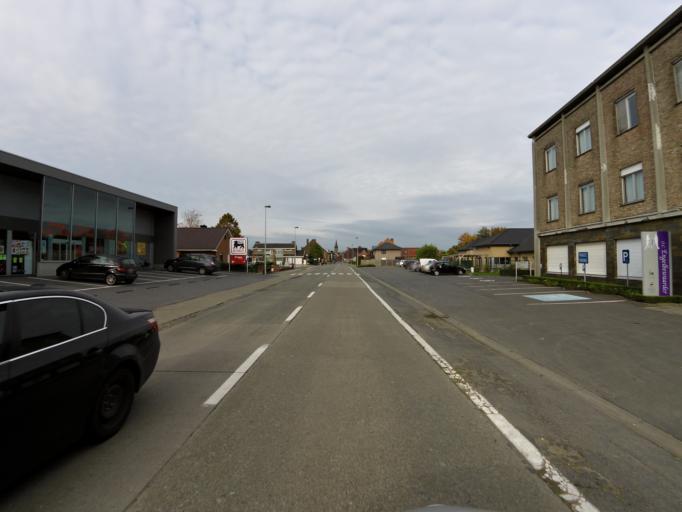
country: BE
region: Flanders
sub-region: Provincie West-Vlaanderen
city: Torhout
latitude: 51.1131
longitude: 3.0916
